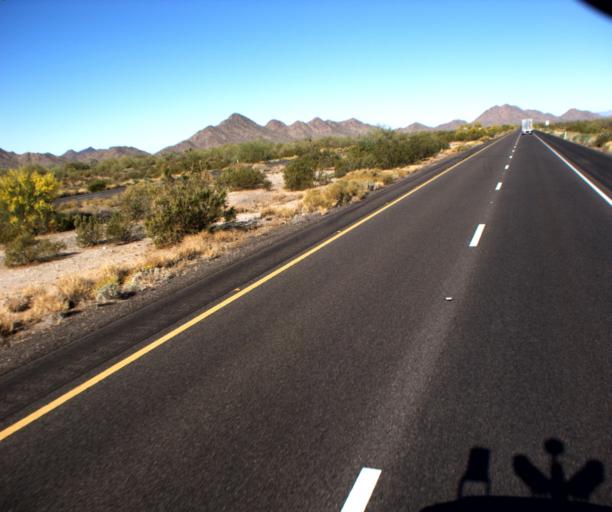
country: US
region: Arizona
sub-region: Maricopa County
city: Gila Bend
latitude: 32.8929
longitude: -112.4907
